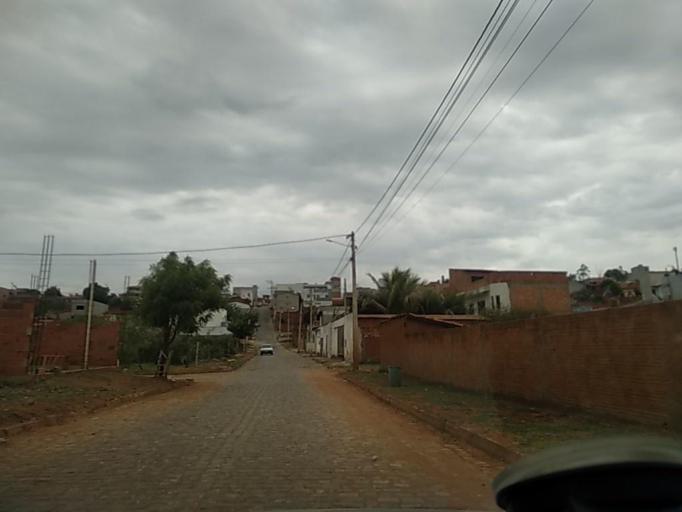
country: BR
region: Bahia
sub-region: Caetite
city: Caetite
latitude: -14.0534
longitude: -42.4781
